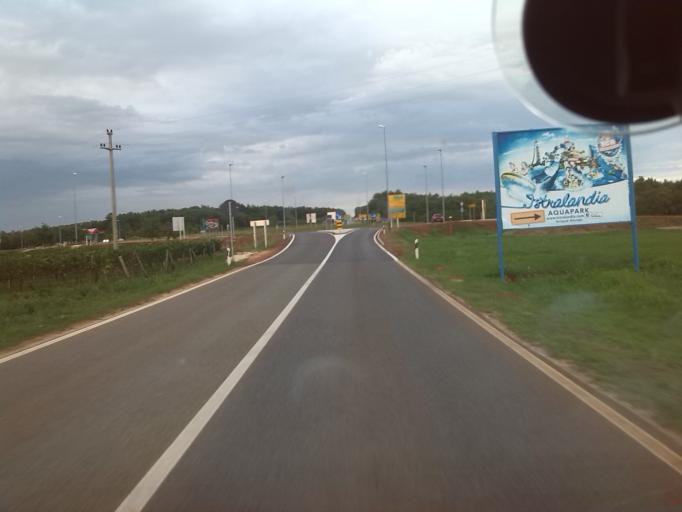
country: HR
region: Istarska
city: Novigrad
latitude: 45.3516
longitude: 13.6158
